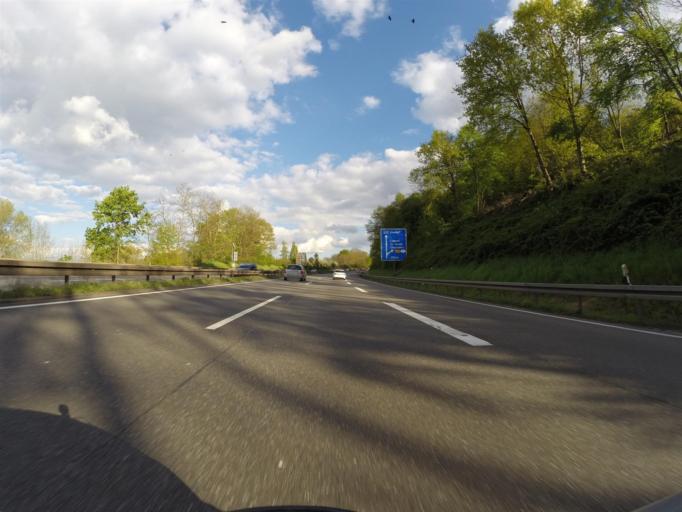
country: DE
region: Saarland
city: Saarlouis
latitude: 49.2989
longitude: 6.7502
